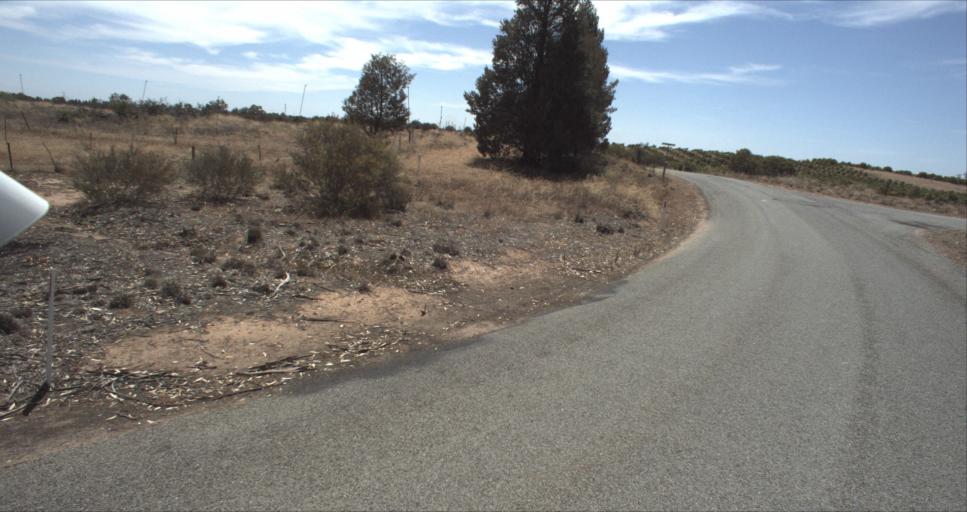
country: AU
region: New South Wales
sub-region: Leeton
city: Leeton
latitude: -34.6695
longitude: 146.4462
